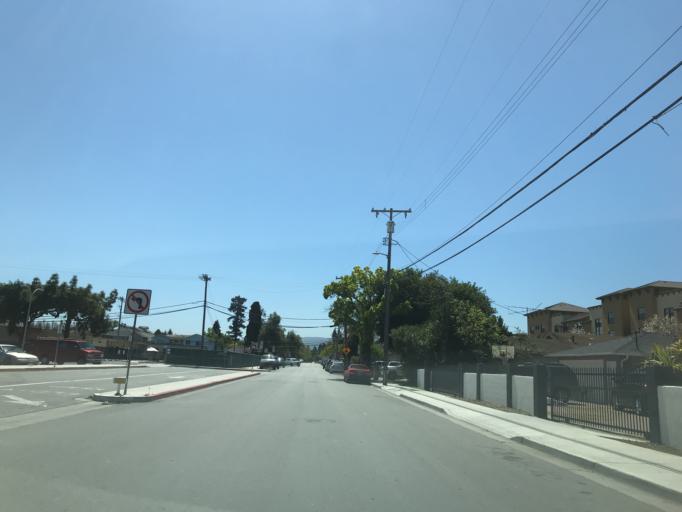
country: US
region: California
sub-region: San Mateo County
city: East Palo Alto
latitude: 37.4621
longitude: -122.1347
